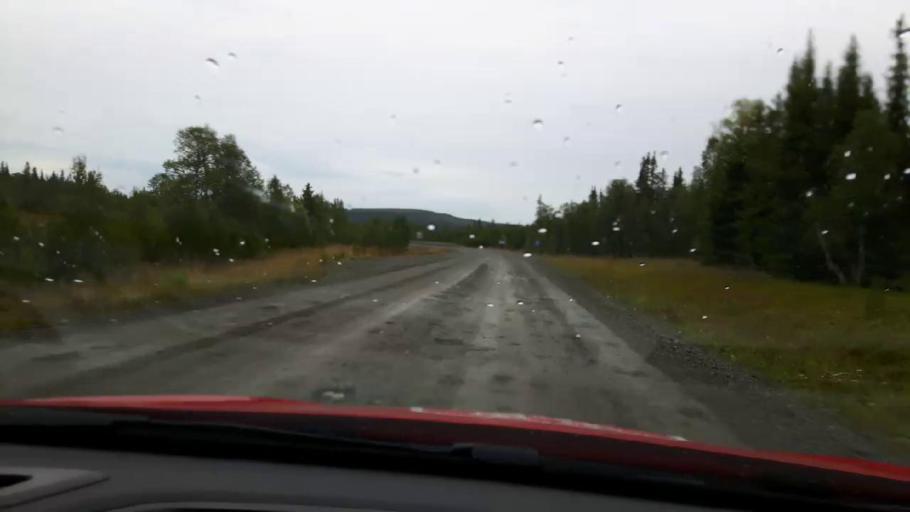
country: NO
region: Nord-Trondelag
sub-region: Meraker
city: Meraker
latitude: 63.5563
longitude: 12.3210
